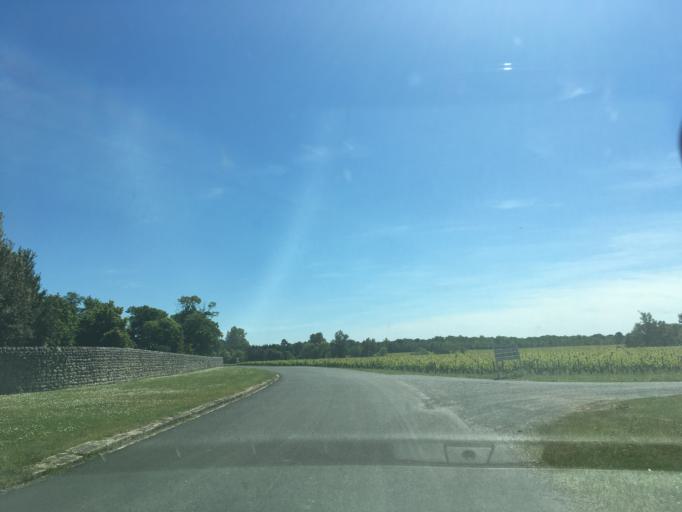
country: FR
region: Aquitaine
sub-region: Departement de la Gironde
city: Lesparre-Medoc
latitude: 45.3096
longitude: -0.8842
